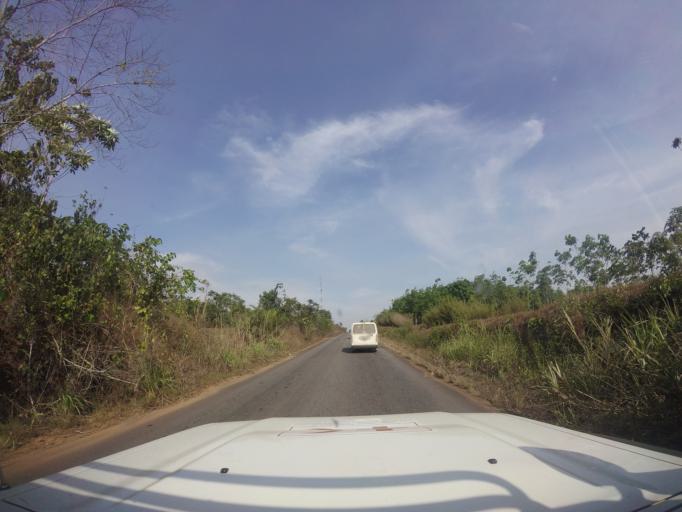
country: LR
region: Bomi
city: Tubmanburg
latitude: 6.6927
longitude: -10.8930
